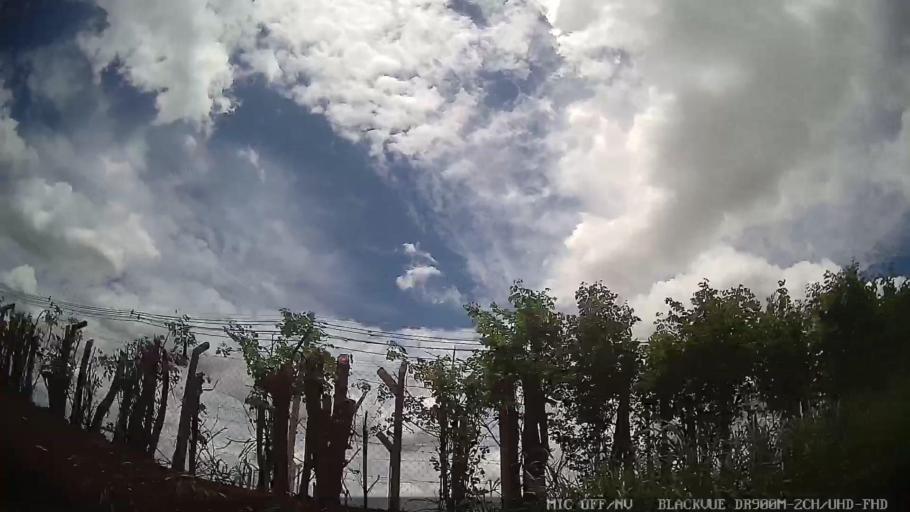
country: BR
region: Sao Paulo
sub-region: Jaguariuna
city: Jaguariuna
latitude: -22.7687
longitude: -47.0122
